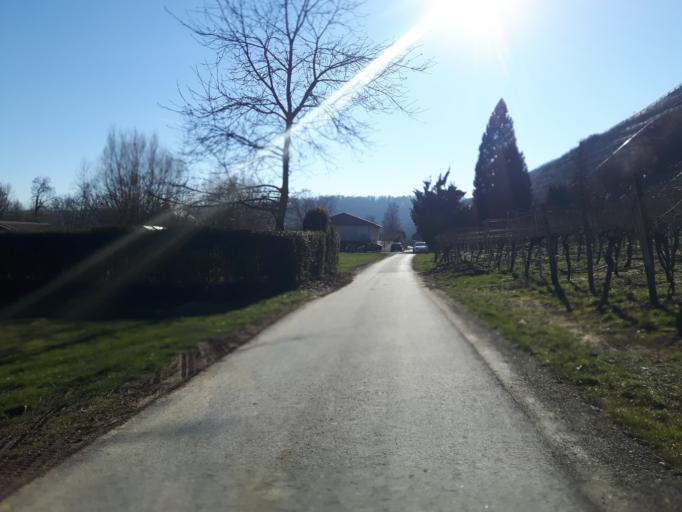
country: DE
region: Baden-Wuerttemberg
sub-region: Regierungsbezirk Stuttgart
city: Lauffen am Neckar
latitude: 49.0729
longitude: 9.1304
